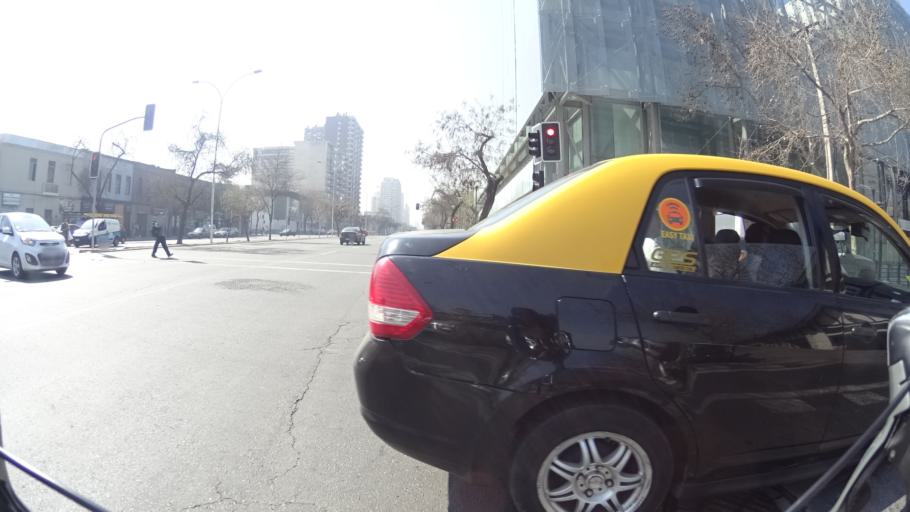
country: CL
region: Santiago Metropolitan
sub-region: Provincia de Santiago
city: Santiago
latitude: -33.4573
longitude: -70.6651
